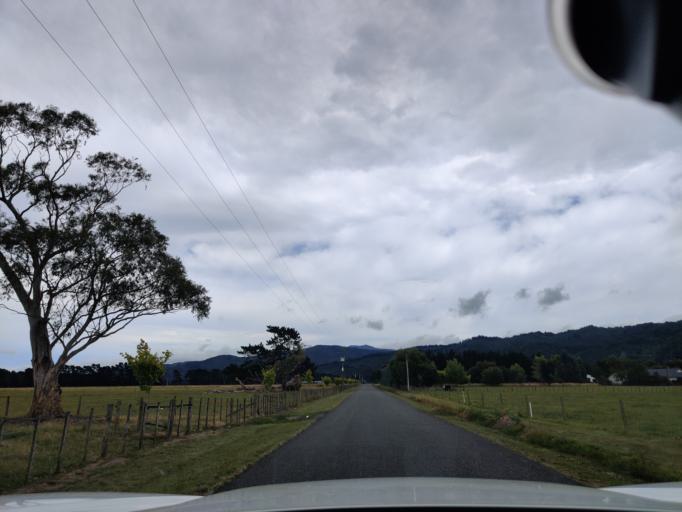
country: NZ
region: Wellington
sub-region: Masterton District
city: Masterton
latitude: -41.0365
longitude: 175.4440
